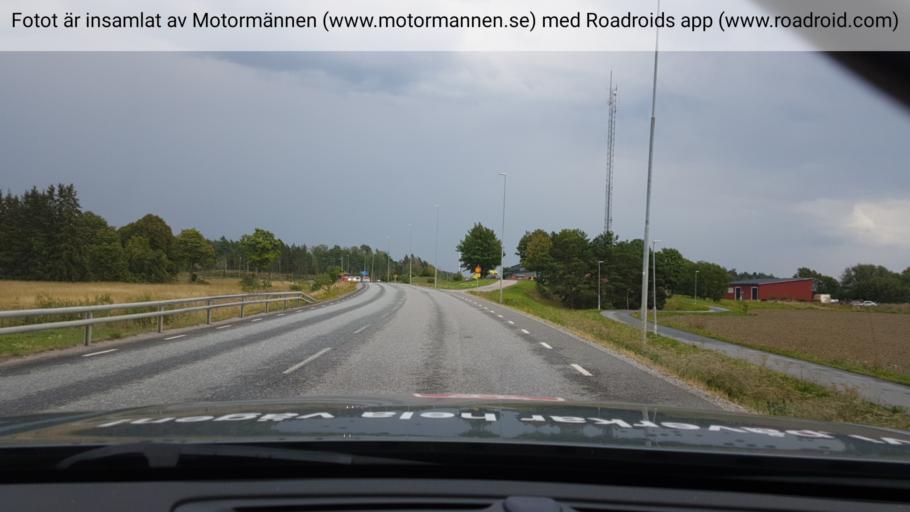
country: SE
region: Stockholm
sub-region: Upplands-Bro Kommun
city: Bro
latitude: 59.5083
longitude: 17.6567
